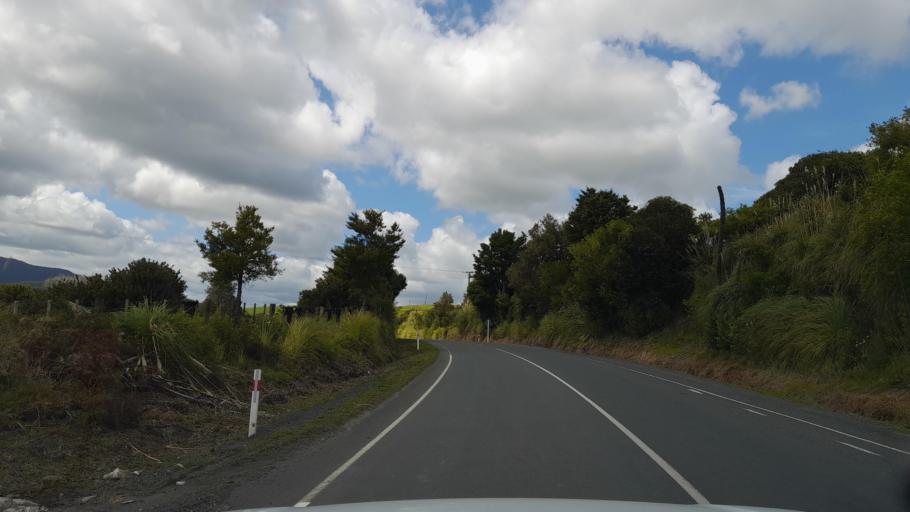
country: NZ
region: Northland
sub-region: Whangarei
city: Maungatapere
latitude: -35.6470
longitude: 174.0415
